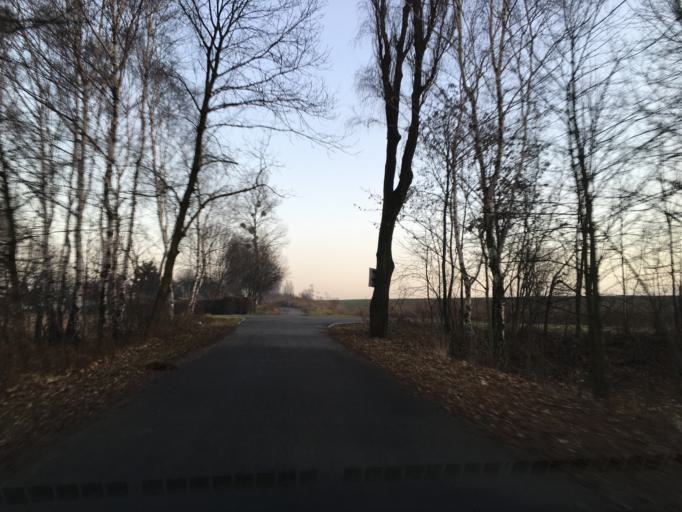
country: PL
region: Silesian Voivodeship
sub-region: Powiat tarnogorski
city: Radzionkow
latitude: 50.3675
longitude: 18.8883
